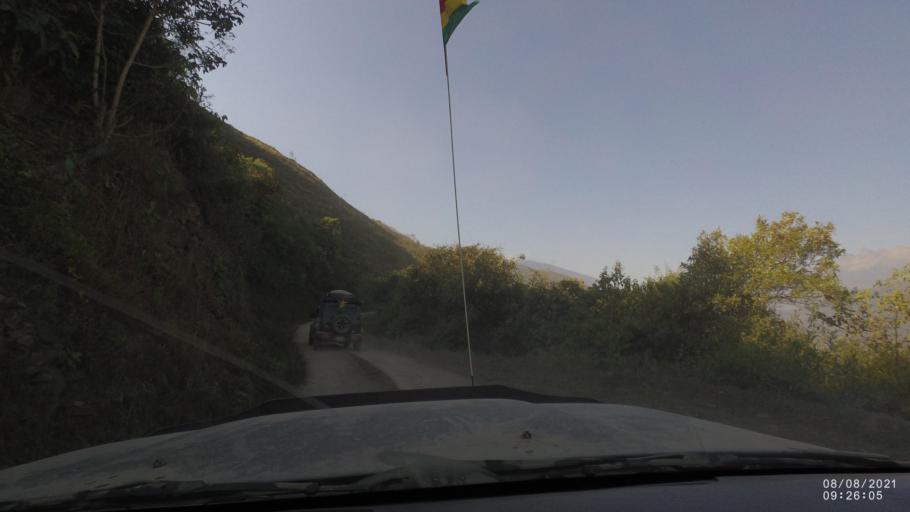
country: BO
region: La Paz
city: Quime
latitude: -16.5853
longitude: -66.7213
